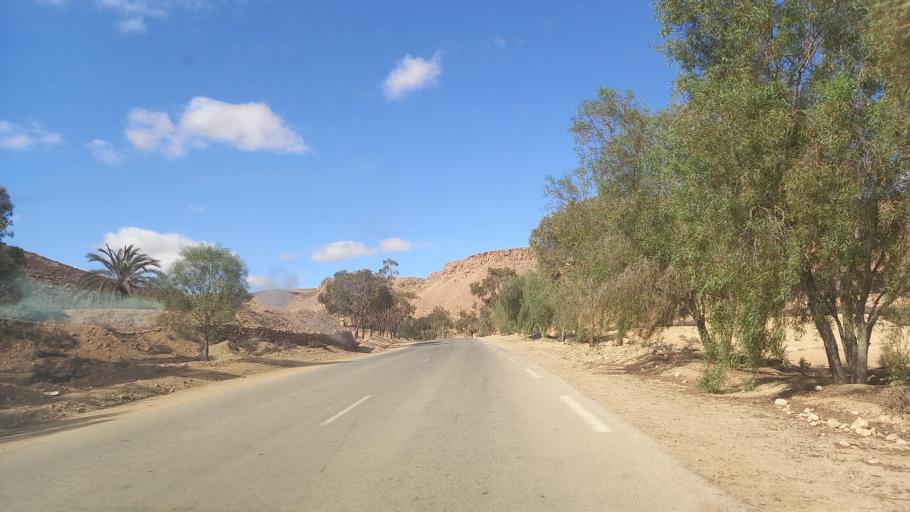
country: TN
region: Tataouine
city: Tataouine
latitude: 32.9173
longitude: 10.2701
